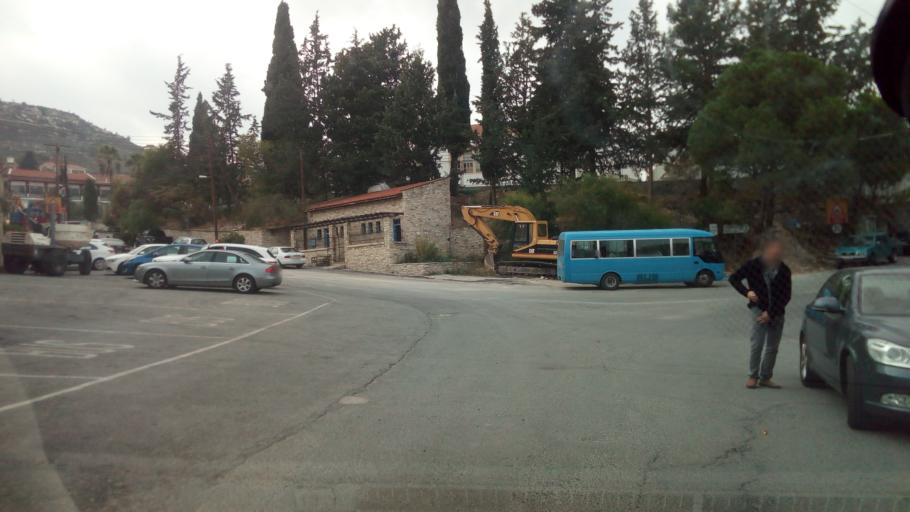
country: CY
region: Lefkosia
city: Lythrodontas
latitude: 34.8680
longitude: 33.3068
